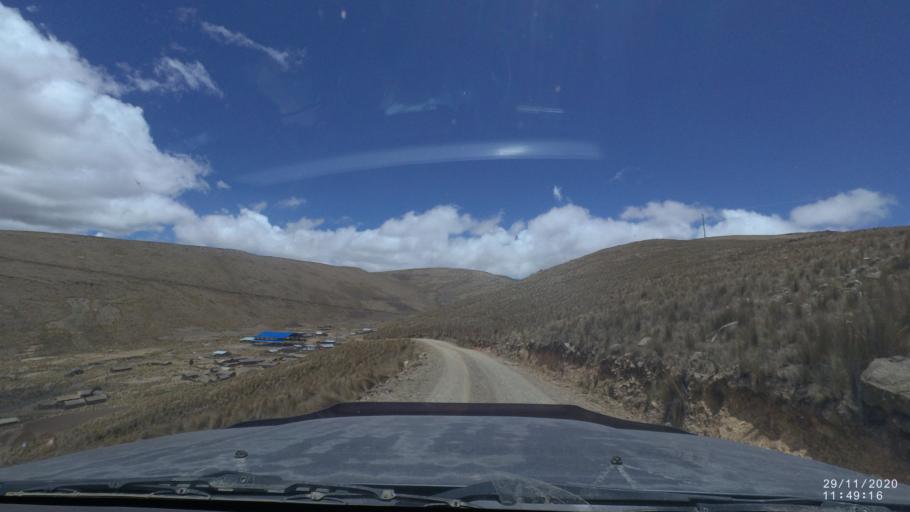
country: BO
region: Cochabamba
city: Cochabamba
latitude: -17.1769
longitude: -66.2602
